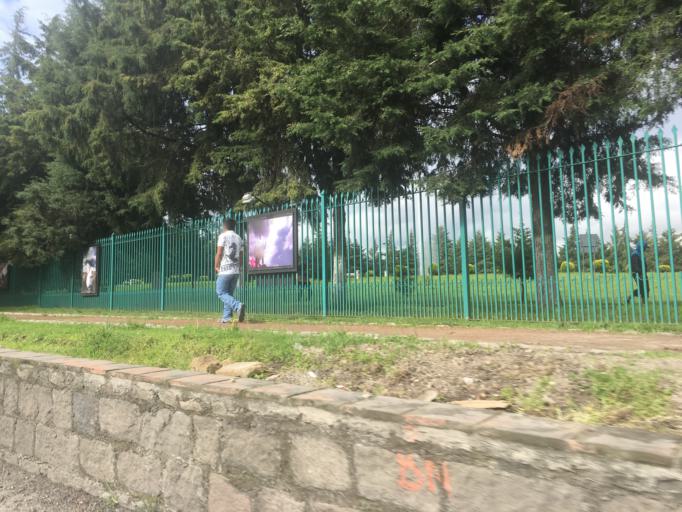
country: MX
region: Morelos
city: Metepec
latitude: 19.2707
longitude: -99.6072
